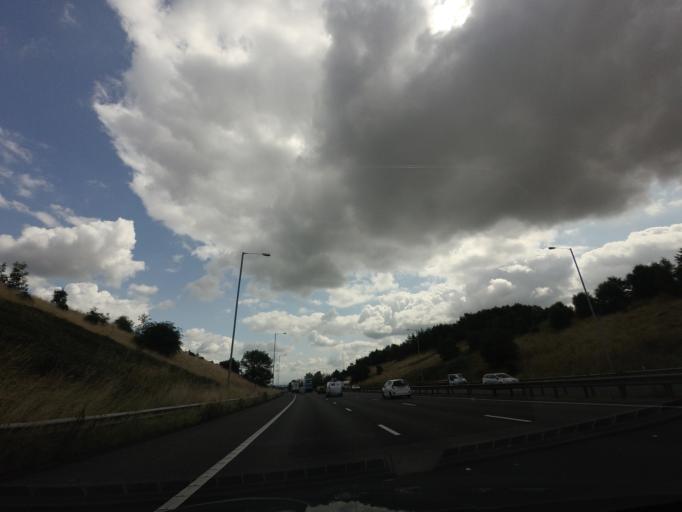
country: GB
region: England
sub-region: St. Helens
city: Billinge
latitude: 53.5131
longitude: -2.6871
